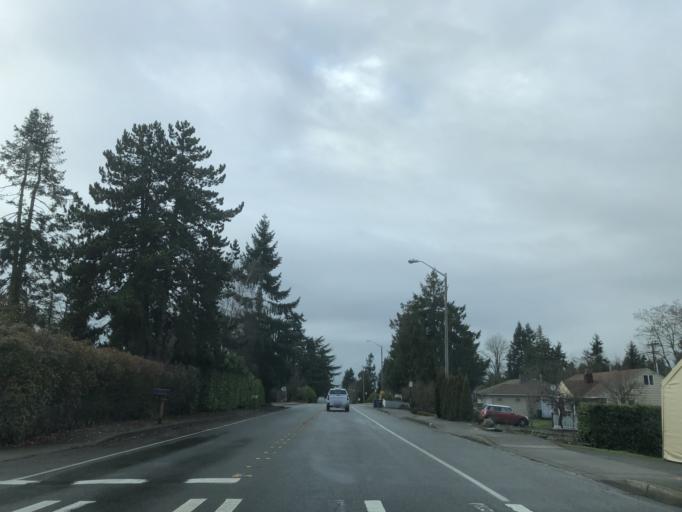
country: US
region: Washington
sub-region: King County
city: SeaTac
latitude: 47.4453
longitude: -122.2815
